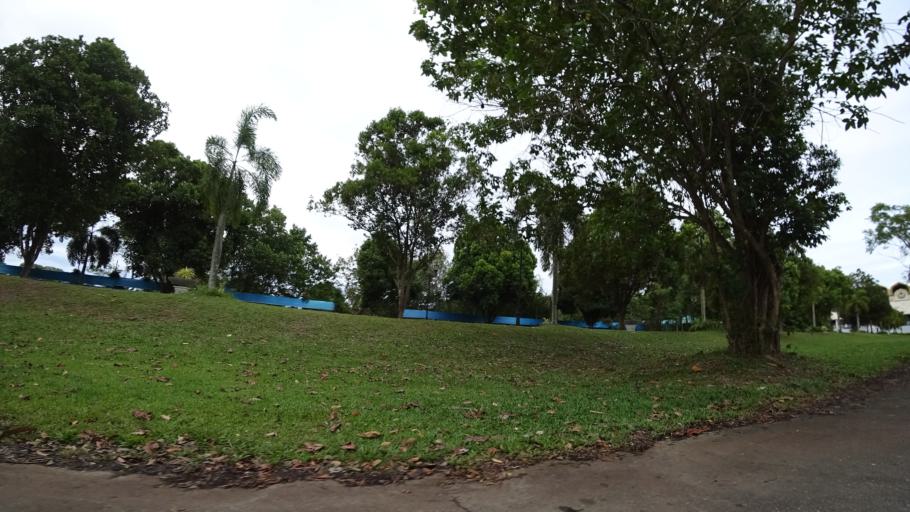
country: BN
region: Brunei and Muara
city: Bandar Seri Begawan
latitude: 4.9289
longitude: 114.9422
